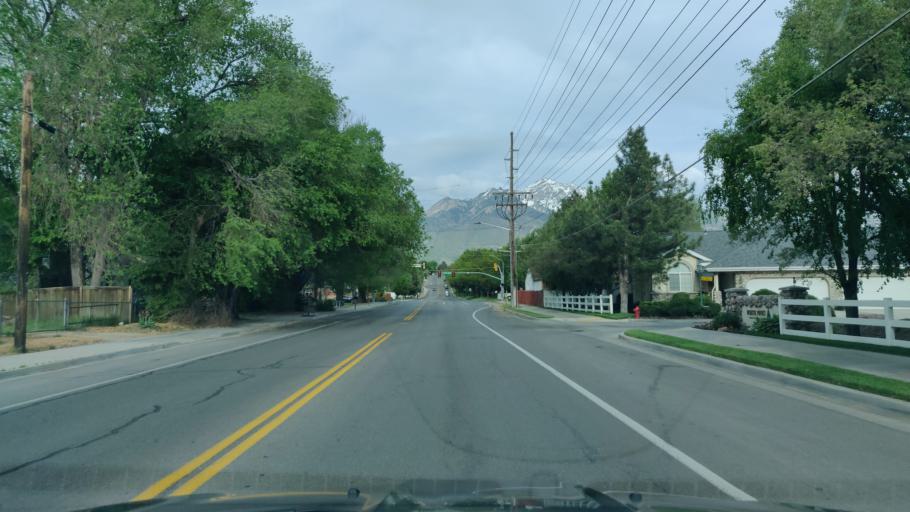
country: US
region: Utah
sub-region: Salt Lake County
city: Sandy City
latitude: 40.6096
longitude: -111.8643
